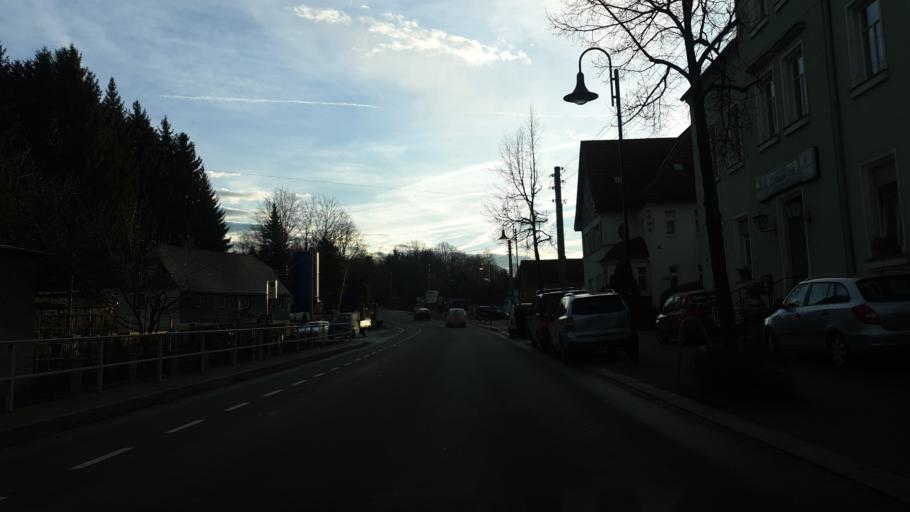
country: DE
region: Saxony
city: Kirchberg
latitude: 50.7913
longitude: 12.7603
